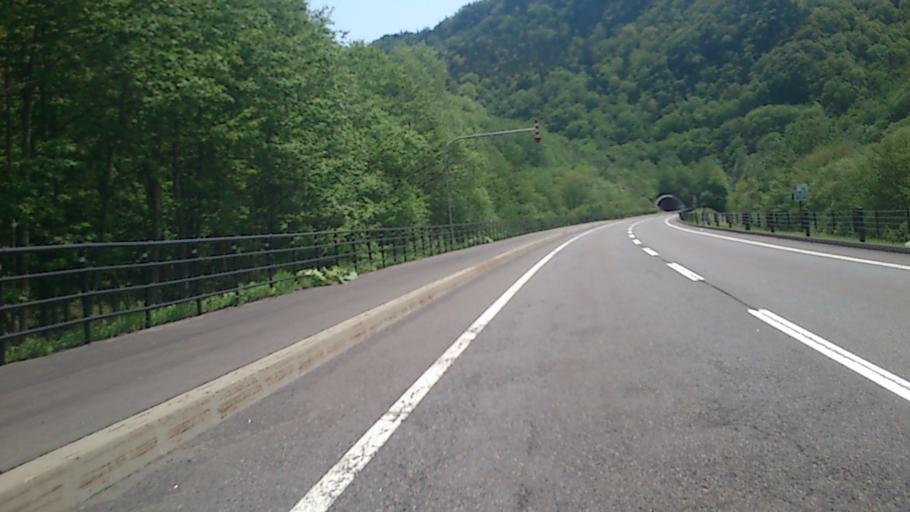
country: JP
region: Hokkaido
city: Otofuke
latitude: 43.3666
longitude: 143.2339
